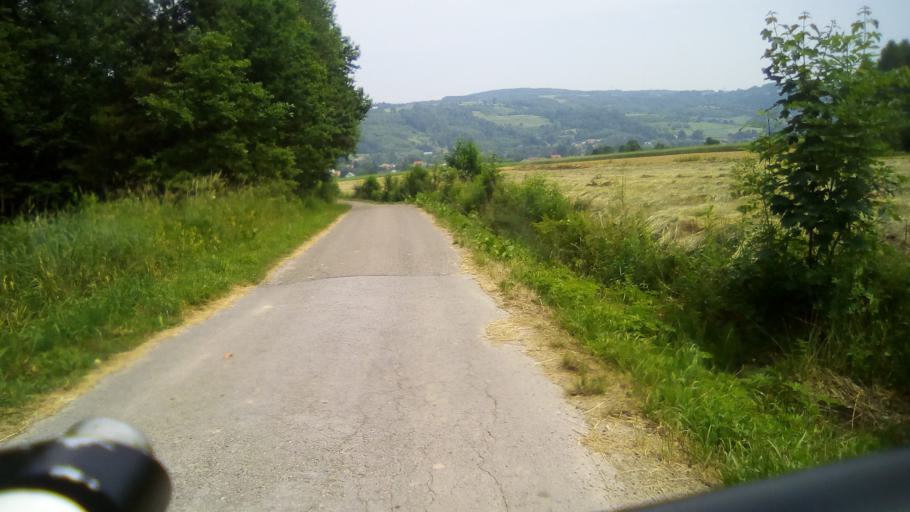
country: PL
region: Subcarpathian Voivodeship
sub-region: Powiat strzyzowski
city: Strzyzow
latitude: 49.8360
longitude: 21.8121
